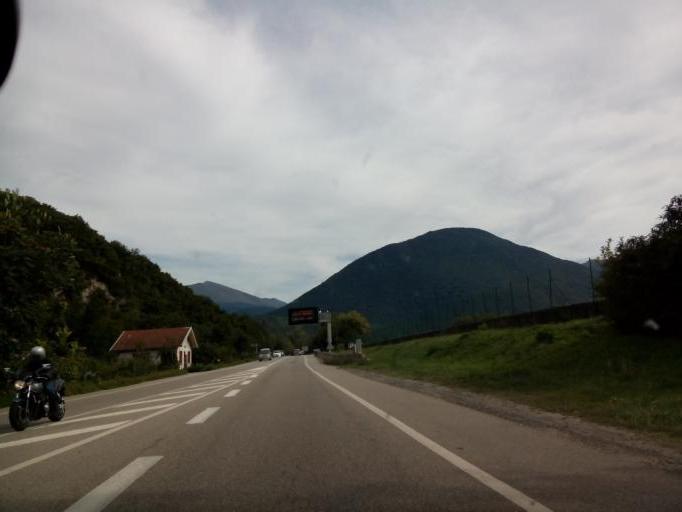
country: FR
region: Rhone-Alpes
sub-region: Departement de l'Isere
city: Champagnier
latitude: 45.0944
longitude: 5.7215
